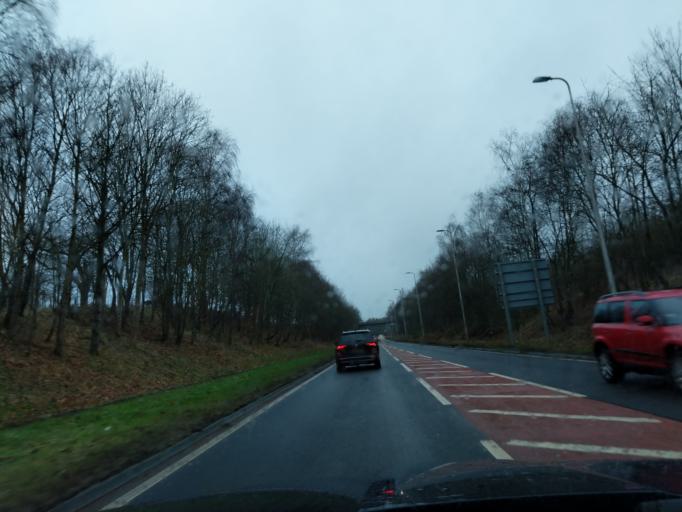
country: GB
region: Scotland
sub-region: The Scottish Borders
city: Melrose
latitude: 55.5993
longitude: -2.7467
